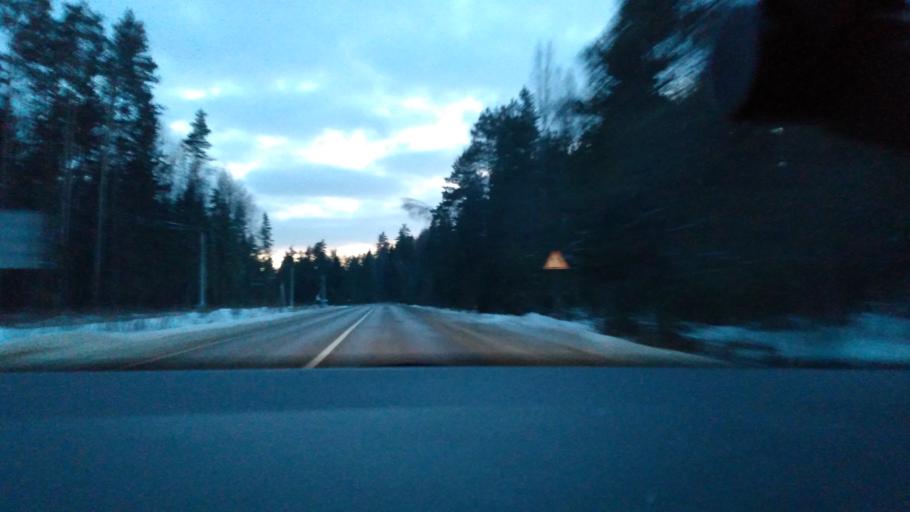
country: RU
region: Moskovskaya
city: Yegor'yevsk
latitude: 55.2709
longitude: 39.0747
